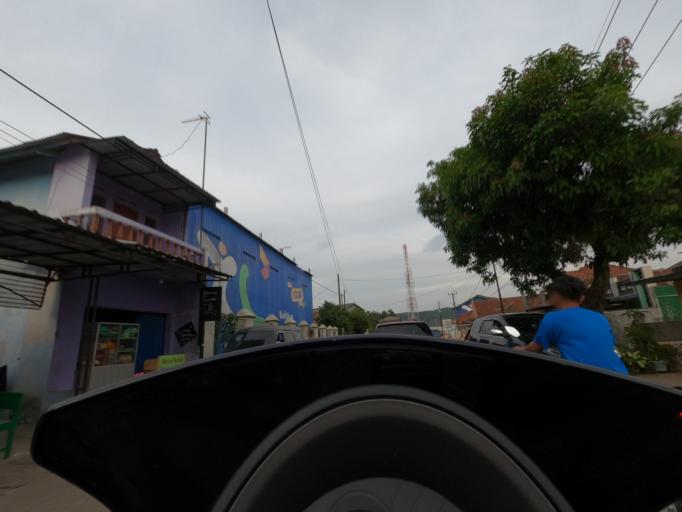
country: ID
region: West Java
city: Lembang
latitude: -6.6569
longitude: 107.7138
